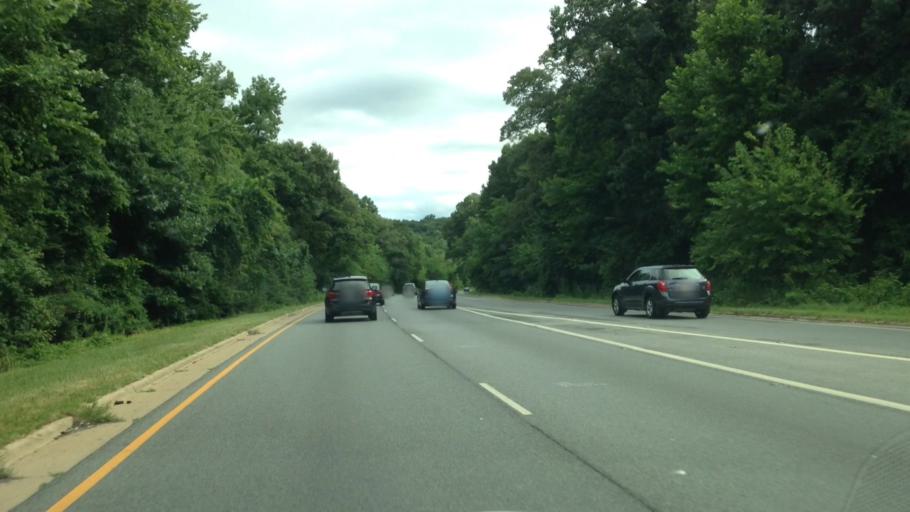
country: US
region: Maryland
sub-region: Prince George's County
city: East Riverdale
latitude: 38.9630
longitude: -76.9044
